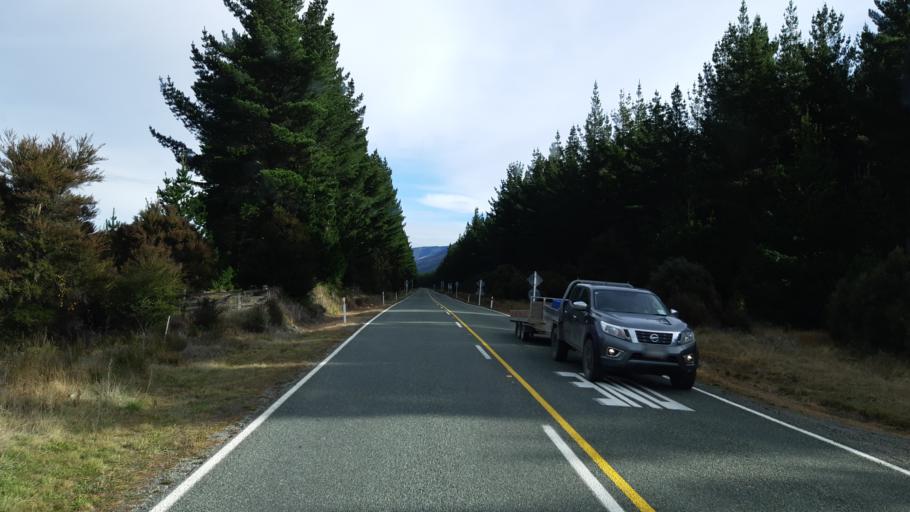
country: NZ
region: Tasman
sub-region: Tasman District
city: Wakefield
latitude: -41.7166
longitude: 173.0787
